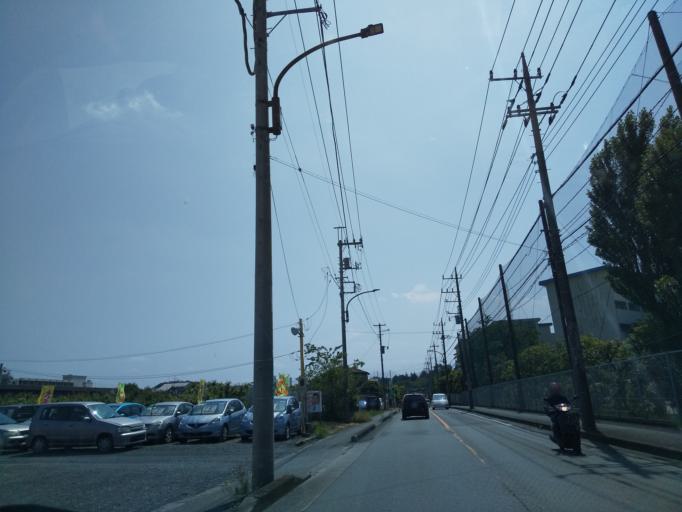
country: JP
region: Kanagawa
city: Zama
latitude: 35.5139
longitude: 139.4022
